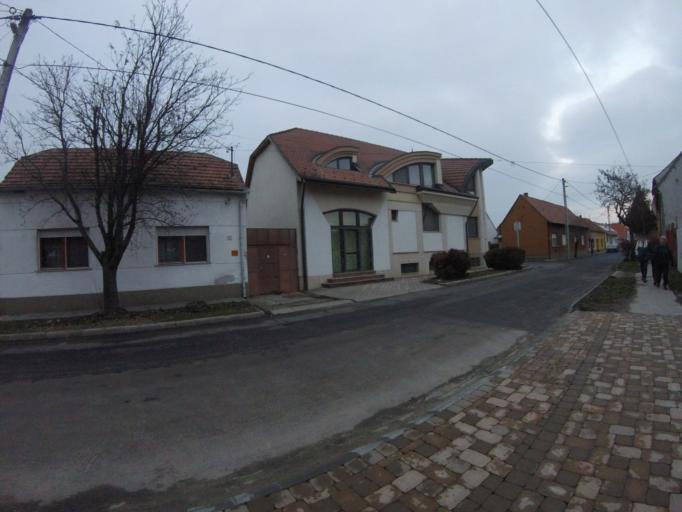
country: HU
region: Baranya
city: Mohacs
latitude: 45.9931
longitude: 18.6898
